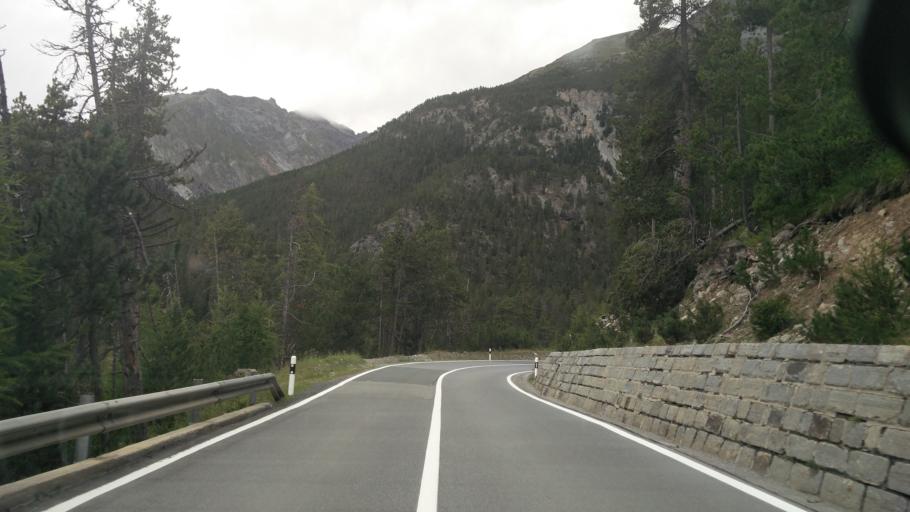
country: CH
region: Grisons
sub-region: Inn District
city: Zernez
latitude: 46.6604
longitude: 10.1974
